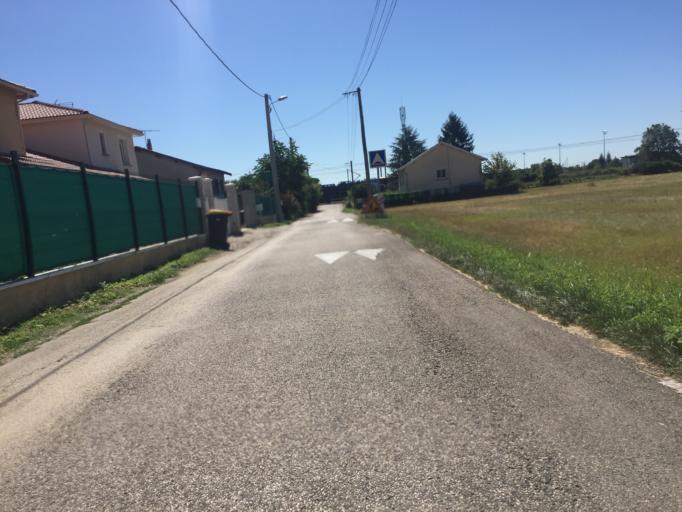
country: FR
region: Rhone-Alpes
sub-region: Departement de l'Ain
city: Saint-Maurice-de-Beynost
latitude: 45.8307
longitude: 4.9870
